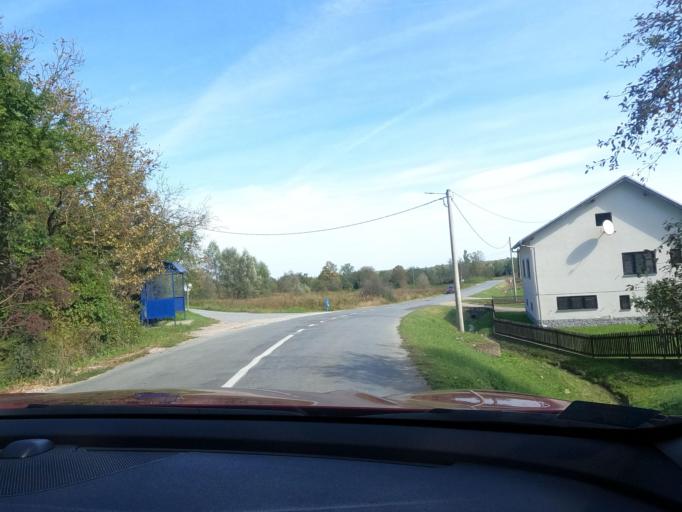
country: HR
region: Sisacko-Moslavacka
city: Petrinja
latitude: 45.4059
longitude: 16.2910
